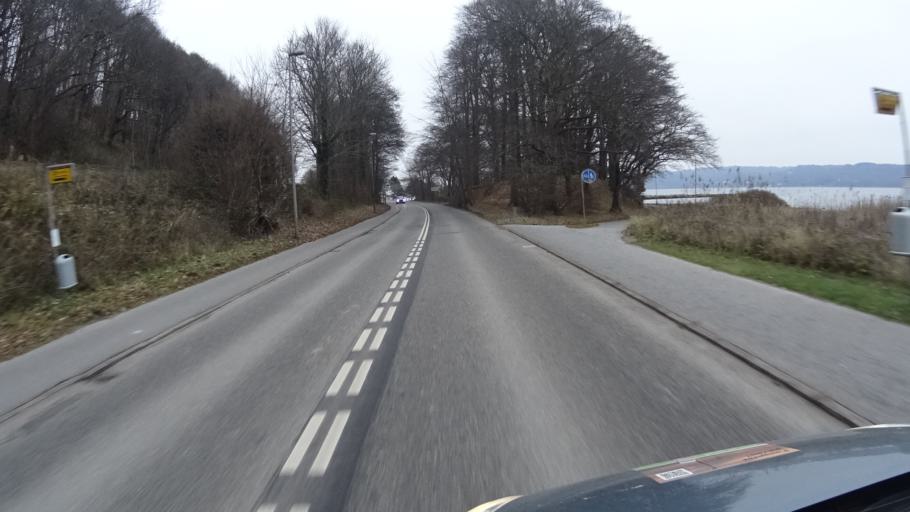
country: DK
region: South Denmark
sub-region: Vejle Kommune
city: Vejle
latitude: 55.7056
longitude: 9.5763
